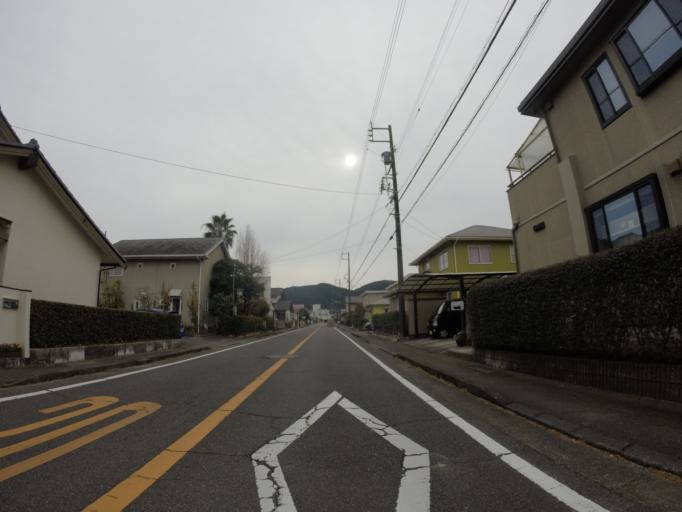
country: JP
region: Shizuoka
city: Fujinomiya
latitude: 35.1886
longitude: 138.6012
